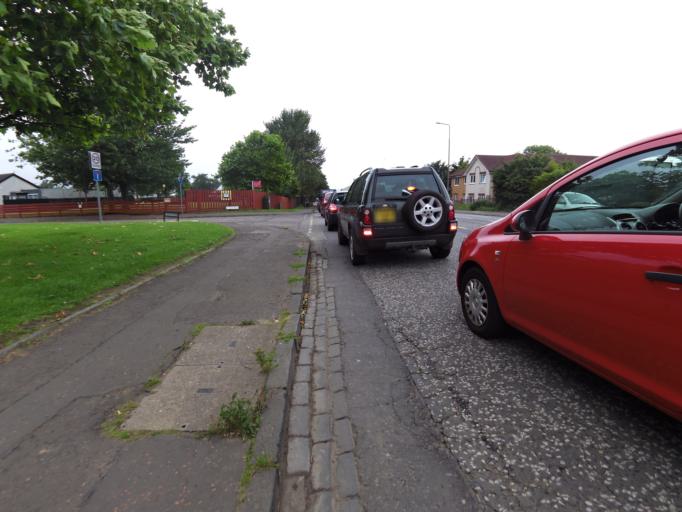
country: GB
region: Scotland
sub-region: West Lothian
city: Seafield
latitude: 55.9335
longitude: -3.1098
